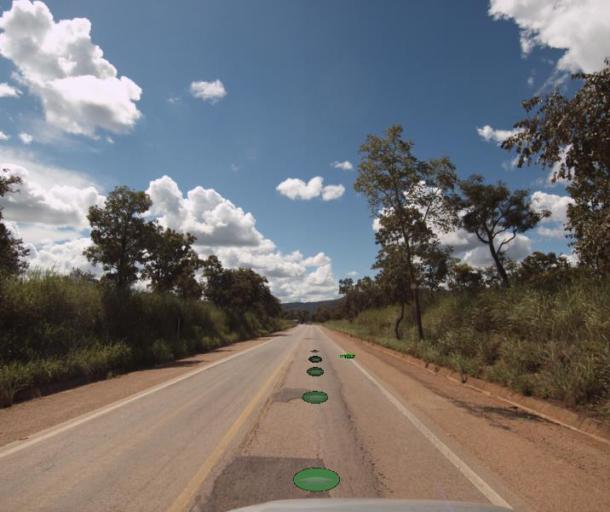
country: BR
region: Goias
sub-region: Porangatu
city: Porangatu
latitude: -13.6830
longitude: -49.0233
